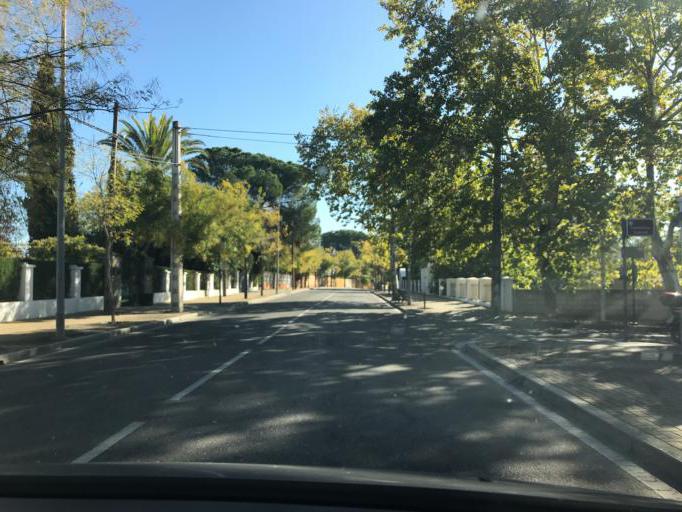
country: ES
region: Andalusia
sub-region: Province of Cordoba
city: Cordoba
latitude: 37.9157
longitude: -4.7994
